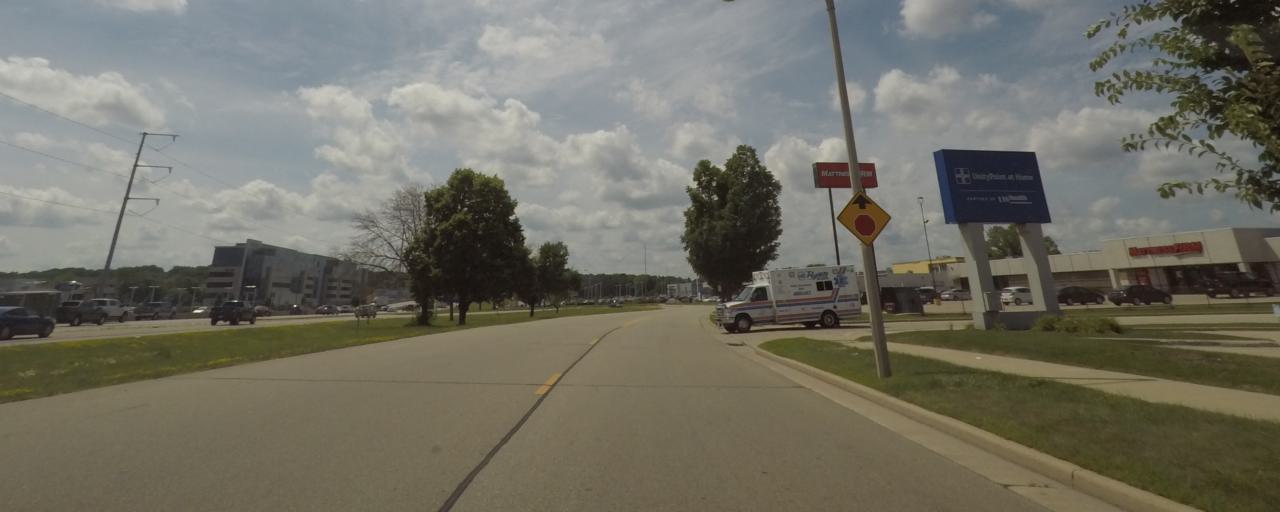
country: US
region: Wisconsin
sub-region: Dane County
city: Madison
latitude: 43.0355
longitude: -89.4165
